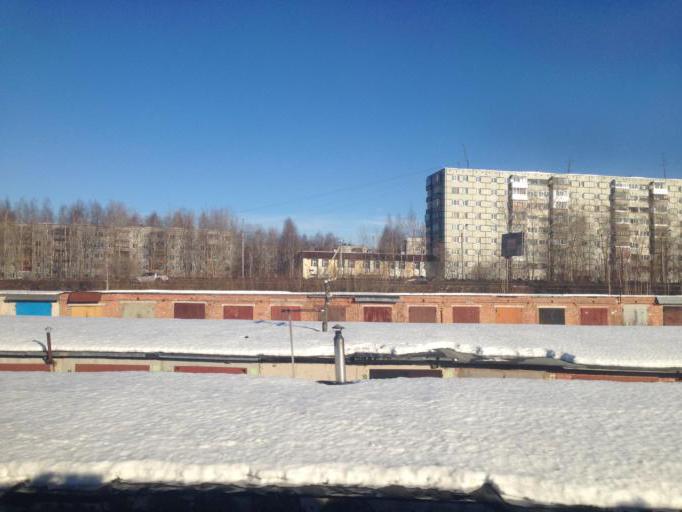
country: RU
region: Komi Republic
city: Ezhva
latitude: 61.7922
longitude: 50.7389
